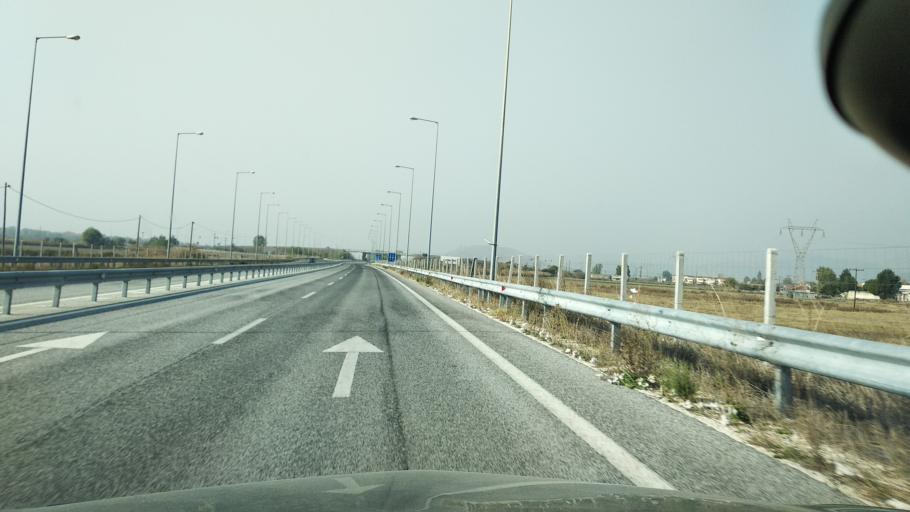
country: GR
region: Thessaly
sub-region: Trikala
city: Farkadona
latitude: 39.5862
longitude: 22.0772
